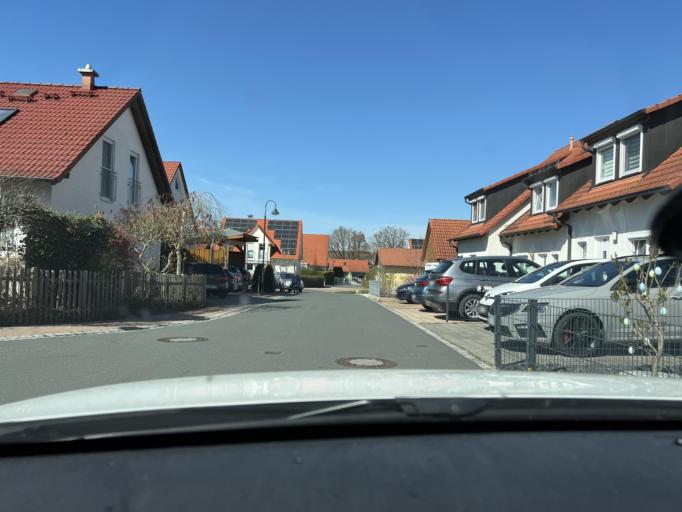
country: DE
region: Bavaria
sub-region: Regierungsbezirk Mittelfranken
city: Wilhermsdorf
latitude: 49.4756
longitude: 10.7201
